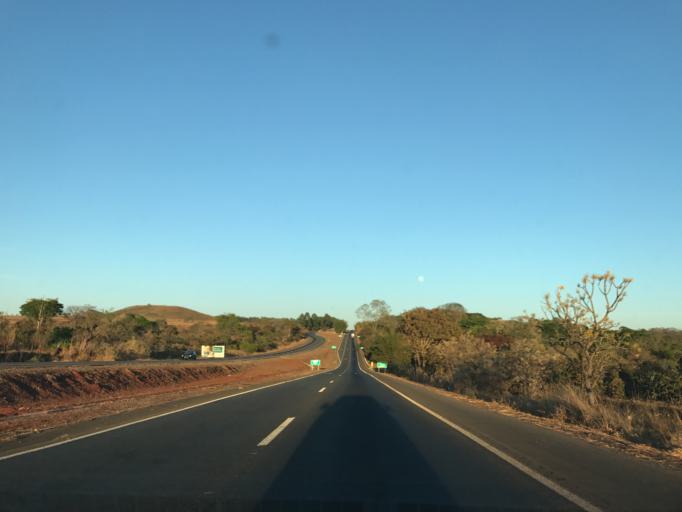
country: BR
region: Goias
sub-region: Anapolis
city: Anapolis
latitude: -16.3134
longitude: -48.8365
